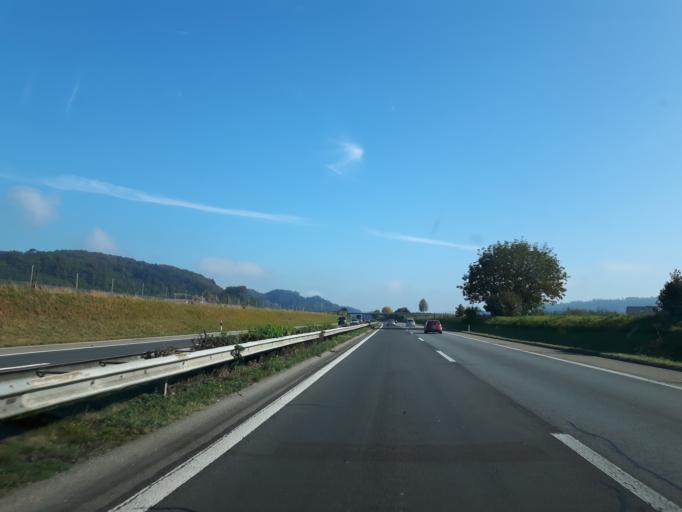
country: CH
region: Lucerne
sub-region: Willisau District
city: Wauwil
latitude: 47.2059
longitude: 8.0352
